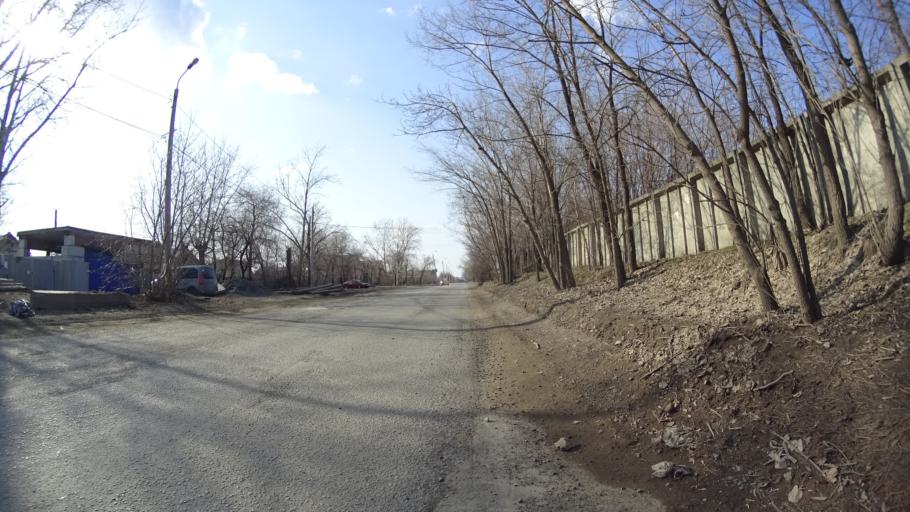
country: RU
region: Chelyabinsk
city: Novosineglazovskiy
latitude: 55.1040
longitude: 61.3425
